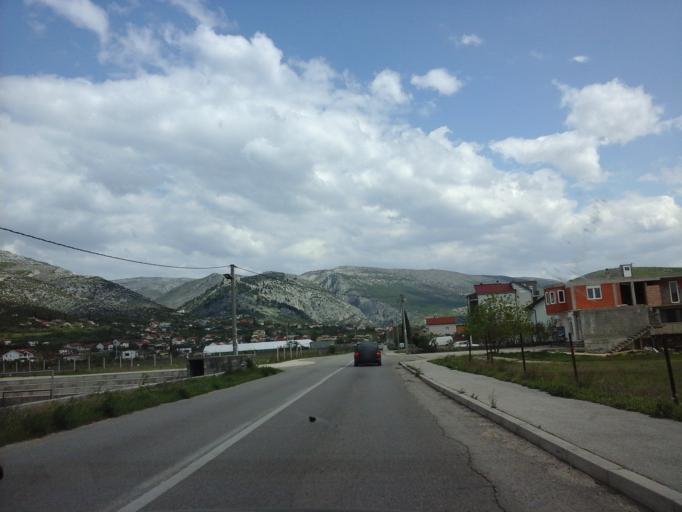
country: BA
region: Federation of Bosnia and Herzegovina
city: Blagaj
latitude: 43.2654
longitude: 17.8743
